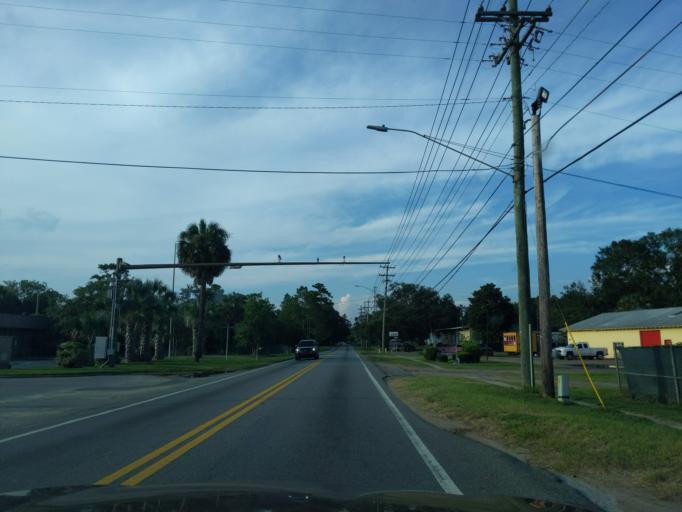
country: US
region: Florida
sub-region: Leon County
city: Tallahassee
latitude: 30.4097
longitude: -84.3046
